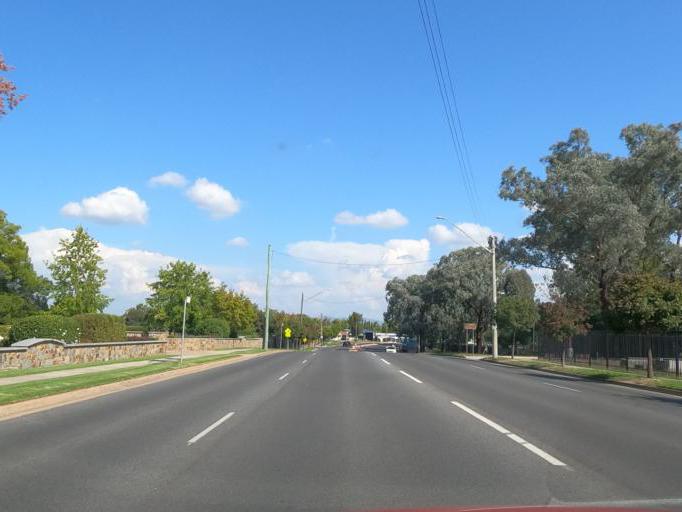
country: AU
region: New South Wales
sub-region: Albury Municipality
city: North Albury
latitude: -36.0608
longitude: 146.9265
